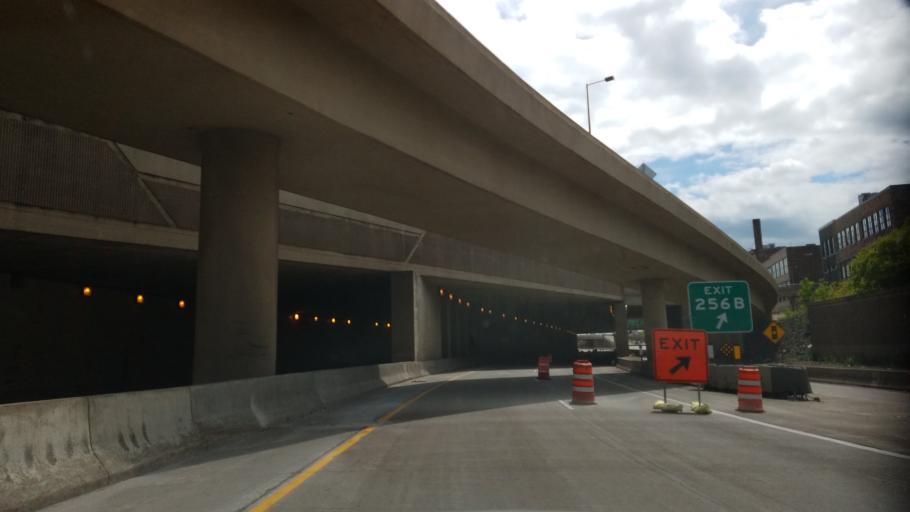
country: US
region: Minnesota
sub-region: Saint Louis County
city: Duluth
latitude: 46.7897
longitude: -92.0934
